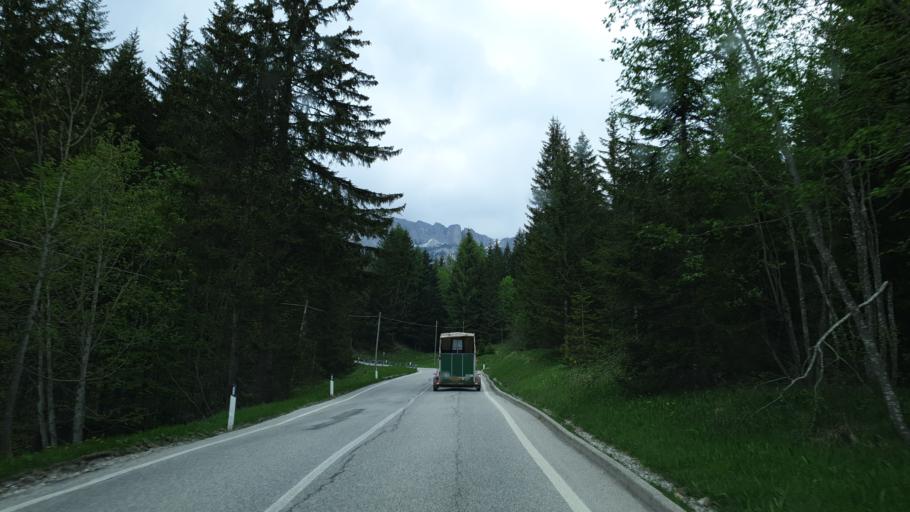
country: IT
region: Veneto
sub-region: Provincia di Belluno
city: San Vito
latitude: 46.5511
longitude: 12.2471
